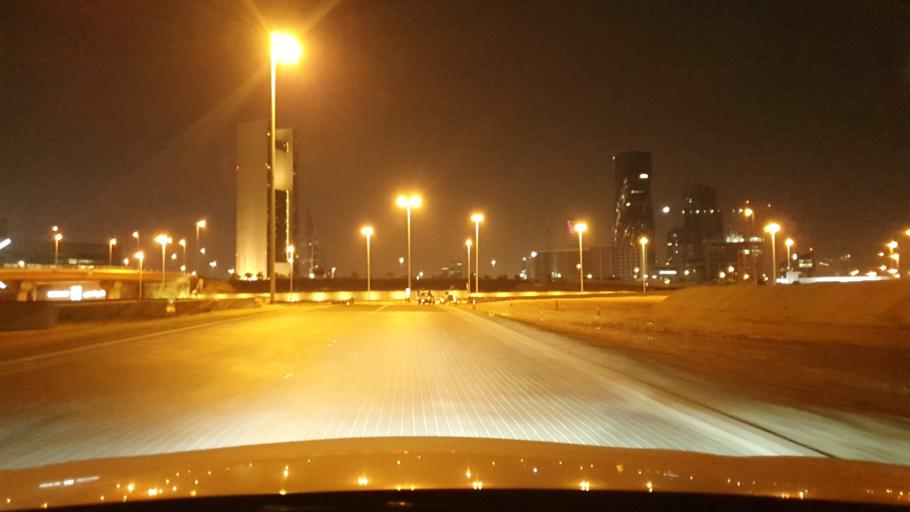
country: BH
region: Muharraq
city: Al Muharraq
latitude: 26.2545
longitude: 50.5813
